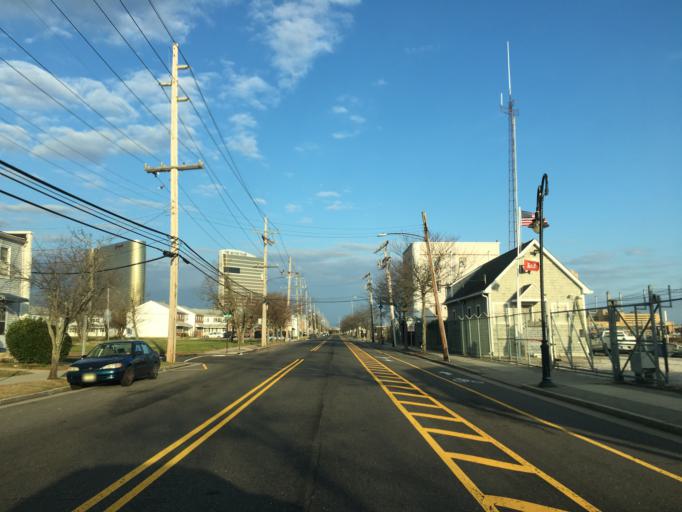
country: US
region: New Jersey
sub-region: Atlantic County
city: Atlantic City
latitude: 39.3717
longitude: -74.4266
